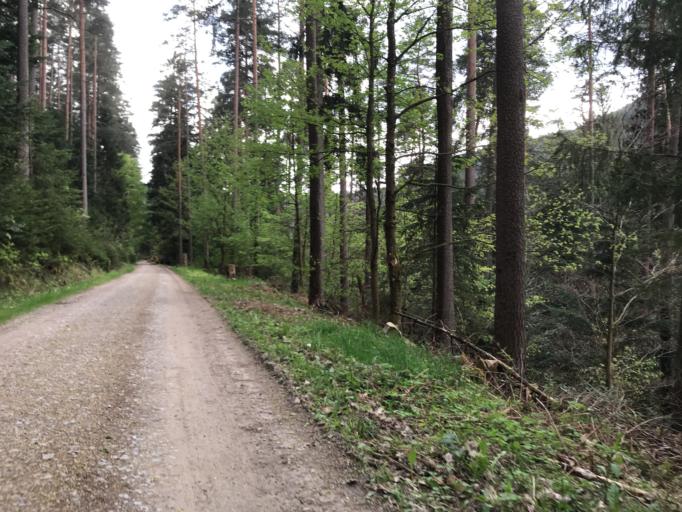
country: DE
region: Baden-Wuerttemberg
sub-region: Karlsruhe Region
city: Baiersbronn
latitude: 48.4948
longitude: 8.3630
